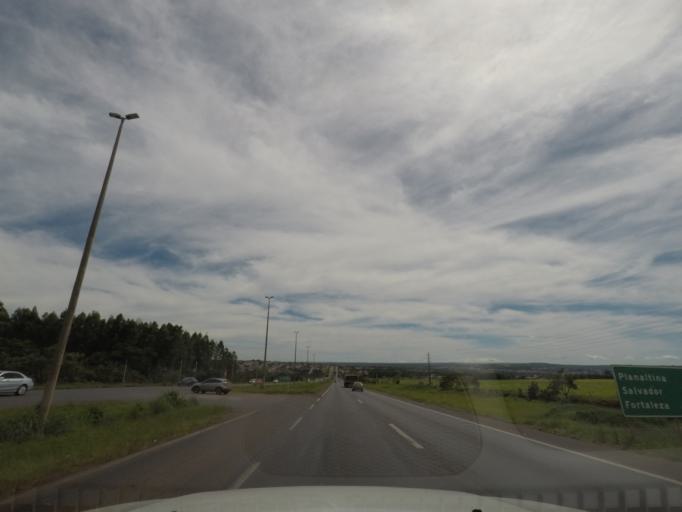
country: BR
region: Goias
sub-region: Planaltina
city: Planaltina
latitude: -15.6132
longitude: -47.7024
